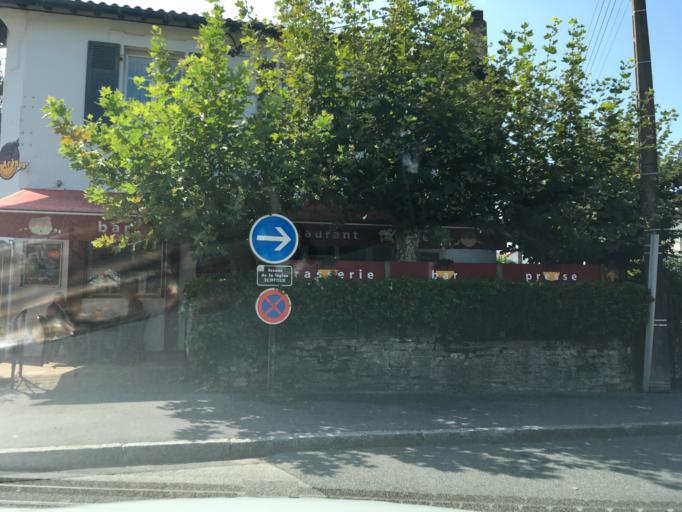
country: FR
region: Aquitaine
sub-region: Departement des Pyrenees-Atlantiques
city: Bayonne
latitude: 43.4919
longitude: -1.4854
